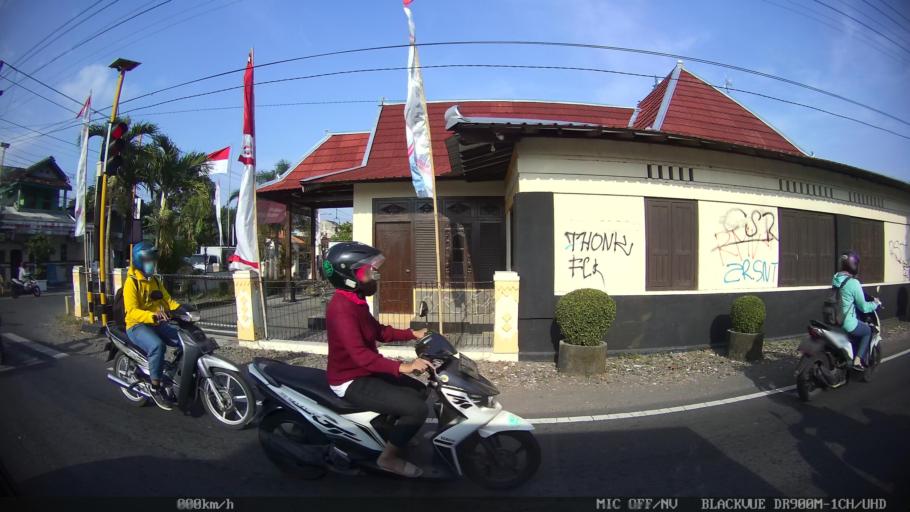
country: ID
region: Daerah Istimewa Yogyakarta
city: Bantul
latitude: -7.8854
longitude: 110.3183
